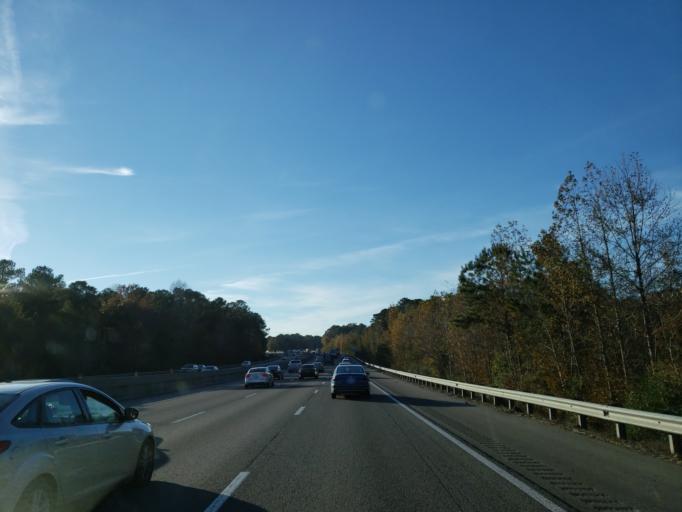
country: US
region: Alabama
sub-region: Tuscaloosa County
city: Coaling
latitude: 33.1904
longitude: -87.3129
